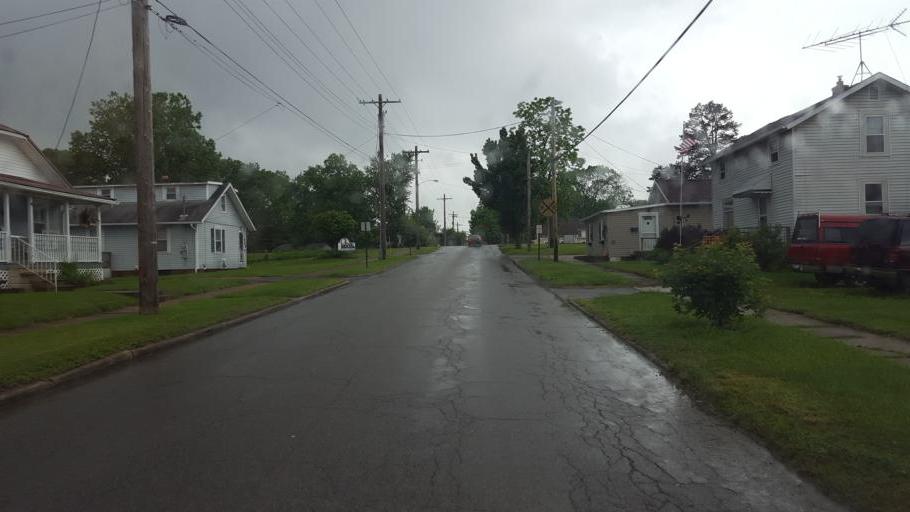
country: US
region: Ohio
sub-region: Ashland County
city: Ashland
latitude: 40.8750
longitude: -82.3057
